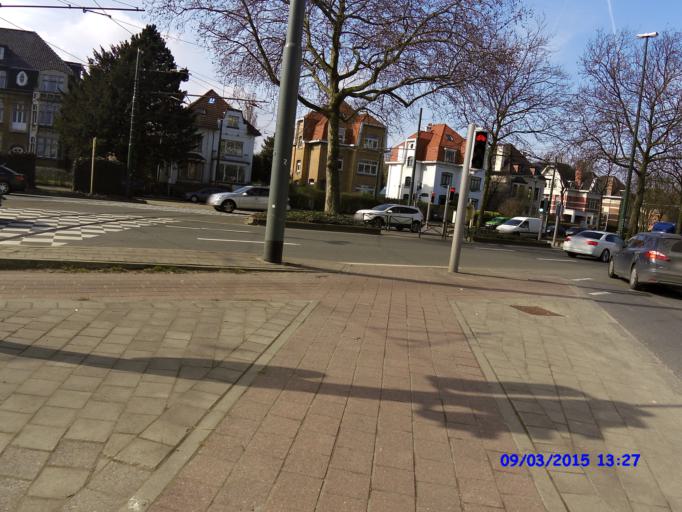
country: BE
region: Brussels Capital
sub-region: Bruxelles-Capitale
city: Brussels
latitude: 50.8581
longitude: 4.3971
